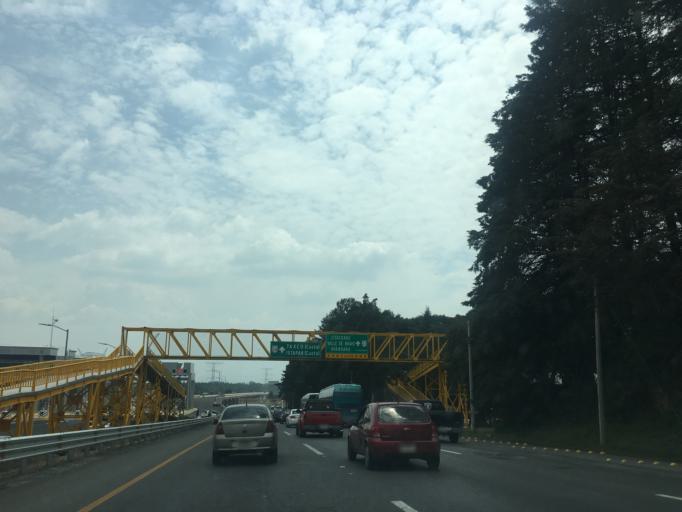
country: MX
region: Mexico
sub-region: Lerma
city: San Miguel Ameyalco
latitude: 19.2915
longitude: -99.4334
